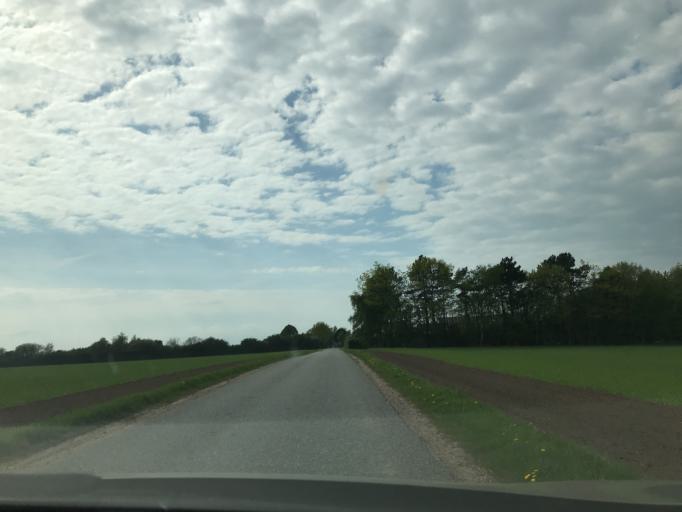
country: DK
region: South Denmark
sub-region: Middelfart Kommune
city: Norre Aby
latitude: 55.3624
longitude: 9.8523
